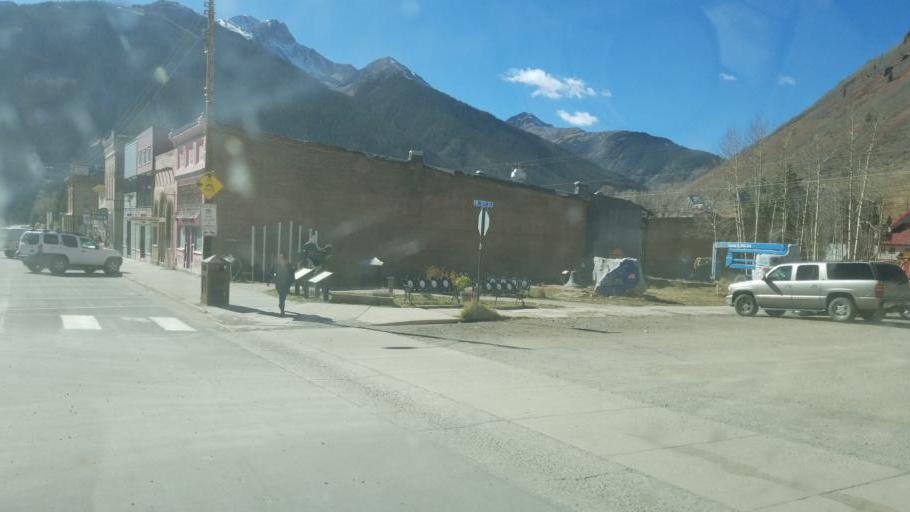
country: US
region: Colorado
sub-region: San Juan County
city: Silverton
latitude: 37.8117
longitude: -107.6645
